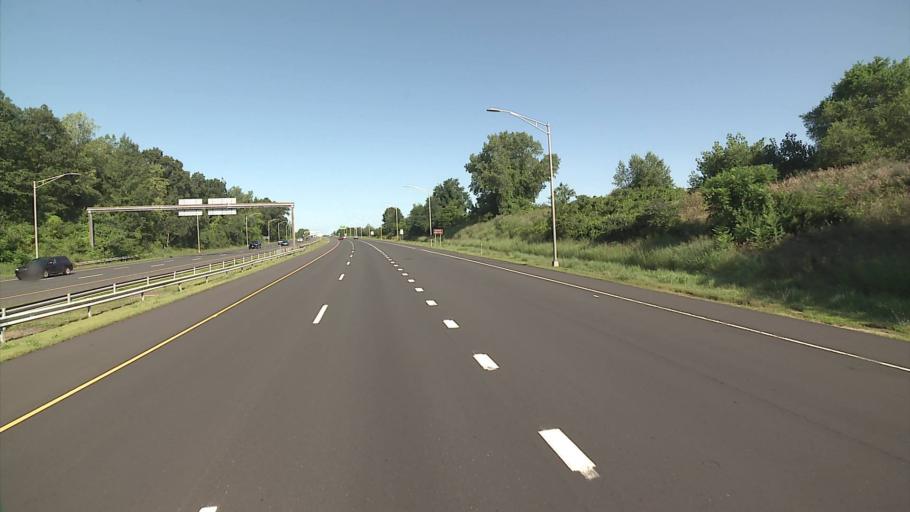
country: US
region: Connecticut
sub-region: Hartford County
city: Windsor Locks
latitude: 41.9022
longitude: -72.6459
